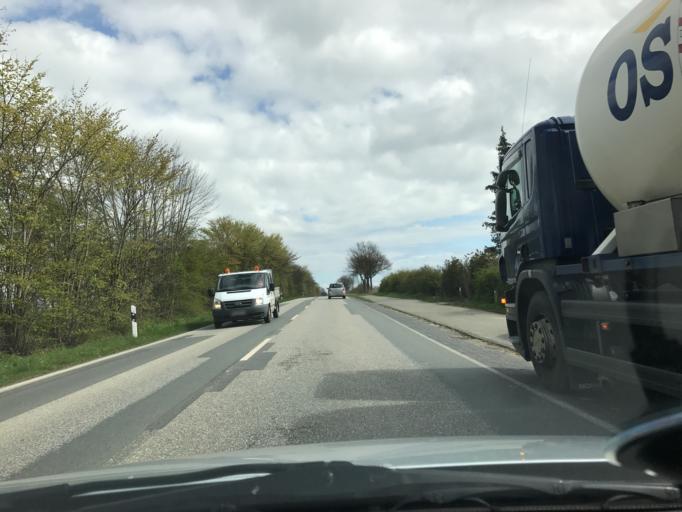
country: DE
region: Schleswig-Holstein
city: Sierksdorf
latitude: 54.0926
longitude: 10.7582
